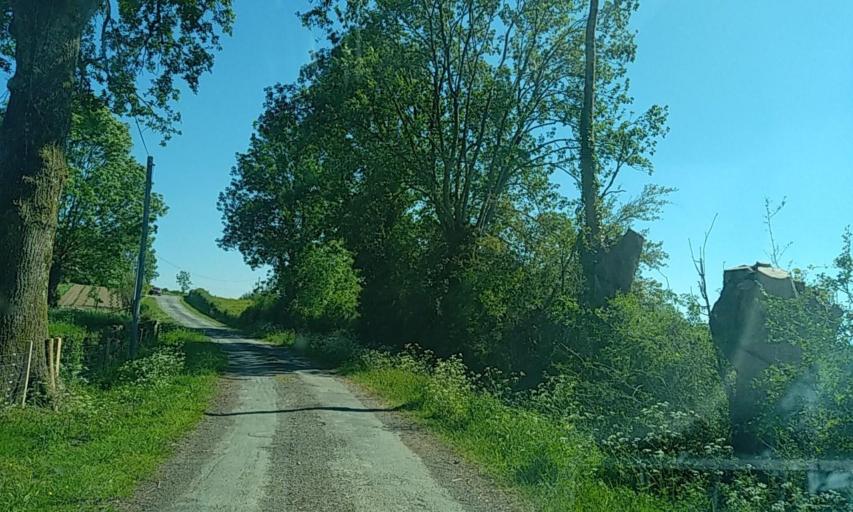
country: FR
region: Poitou-Charentes
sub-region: Departement des Deux-Sevres
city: Boisme
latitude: 46.7949
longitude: -0.4685
